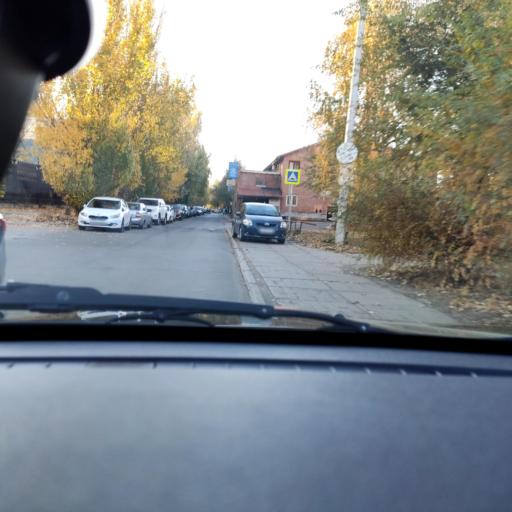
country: RU
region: Samara
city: Tol'yatti
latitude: 53.5095
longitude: 49.2701
